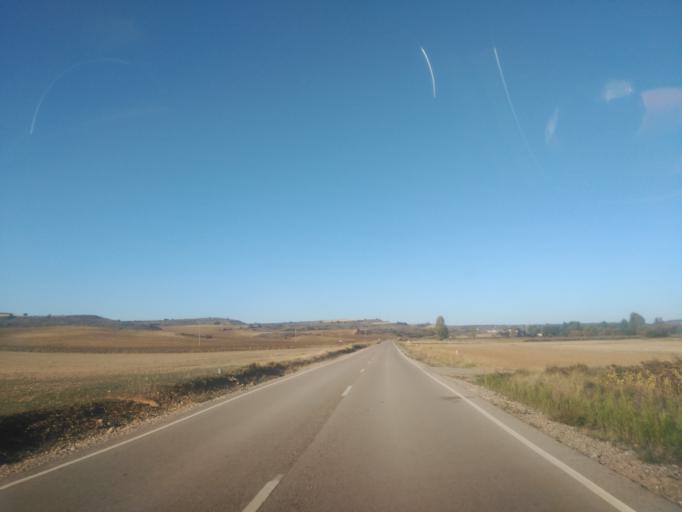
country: ES
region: Castille and Leon
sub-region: Provincia de Soria
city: Espeja de San Marcelino
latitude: 41.7562
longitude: -3.2491
